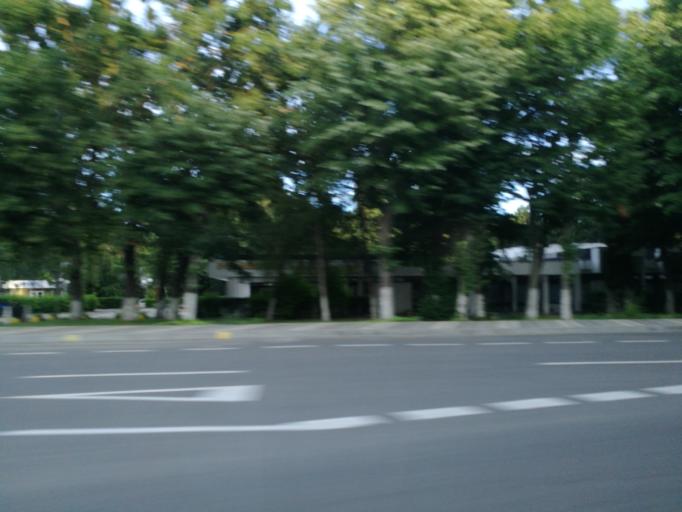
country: RO
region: Constanta
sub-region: Comuna Douazeci si Trei August
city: Douazeci si Trei August
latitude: 43.8813
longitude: 28.6032
